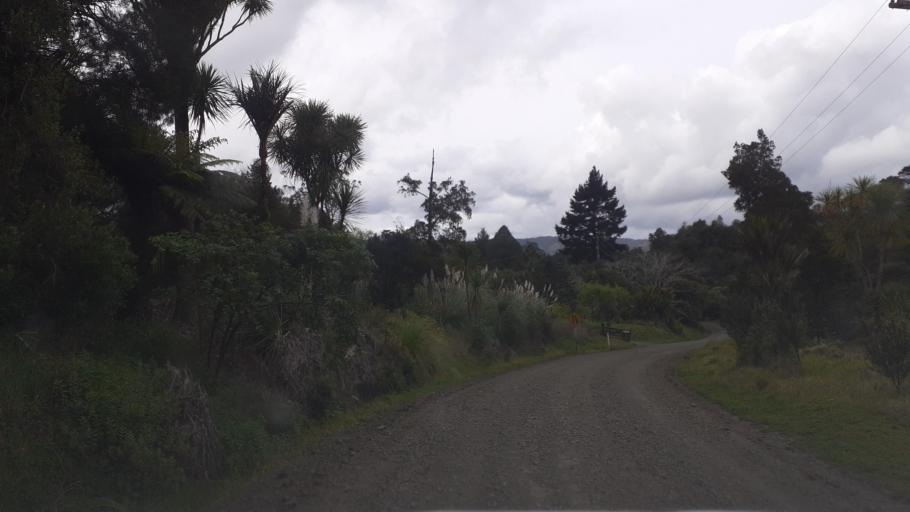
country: NZ
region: Northland
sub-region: Far North District
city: Kaitaia
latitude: -35.5314
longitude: 173.4349
